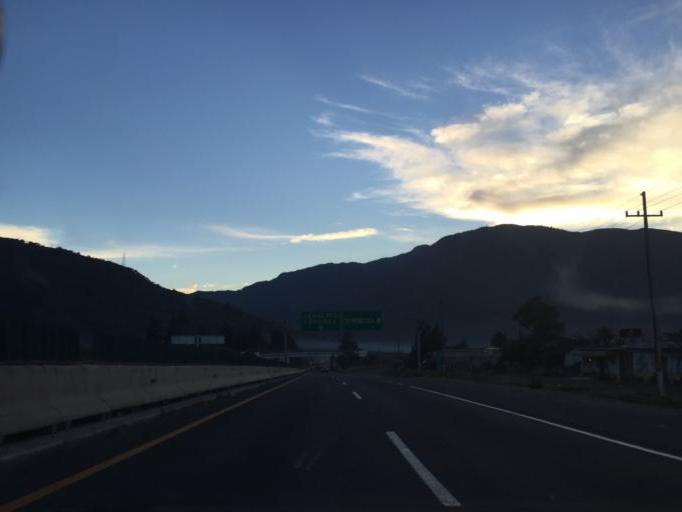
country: MX
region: Veracruz
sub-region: Nogales
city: Agricola Lazaro Cardenas
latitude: 18.8139
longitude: -97.1927
